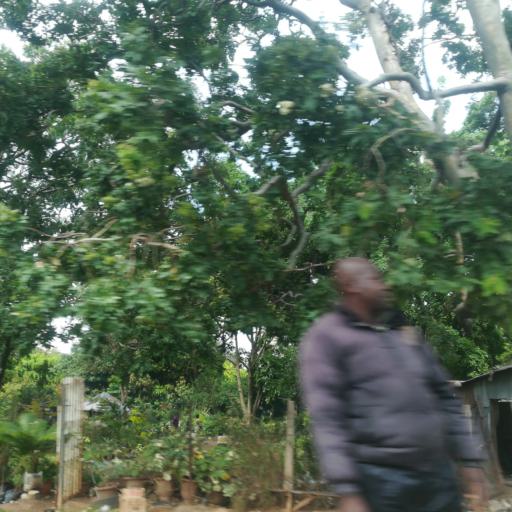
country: NG
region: Plateau
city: Jos
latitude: 9.9104
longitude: 8.8884
